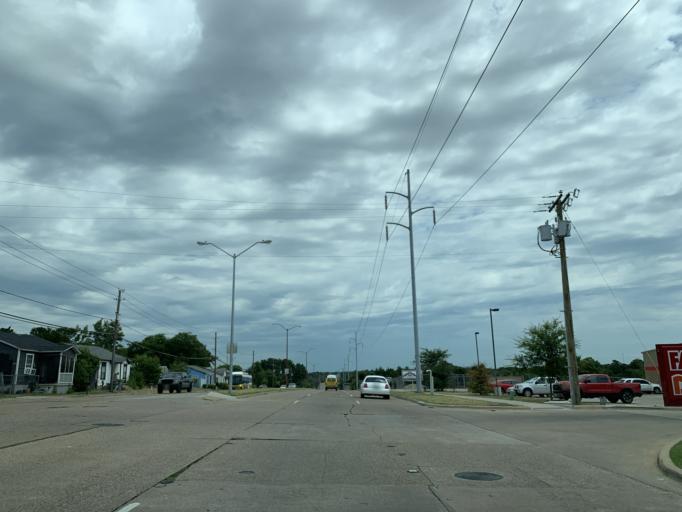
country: US
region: Texas
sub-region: Dallas County
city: DeSoto
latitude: 32.6622
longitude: -96.8216
